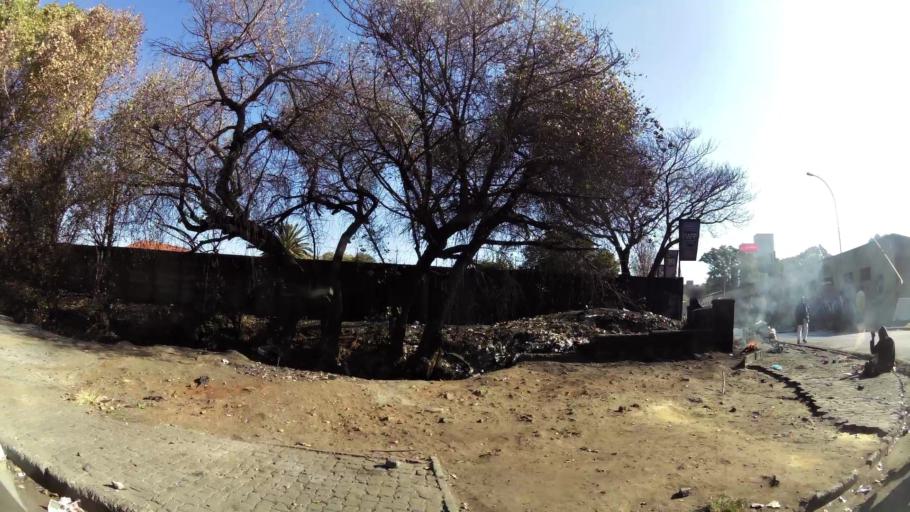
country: ZA
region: Gauteng
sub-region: City of Johannesburg Metropolitan Municipality
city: Johannesburg
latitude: -26.2076
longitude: 28.0604
